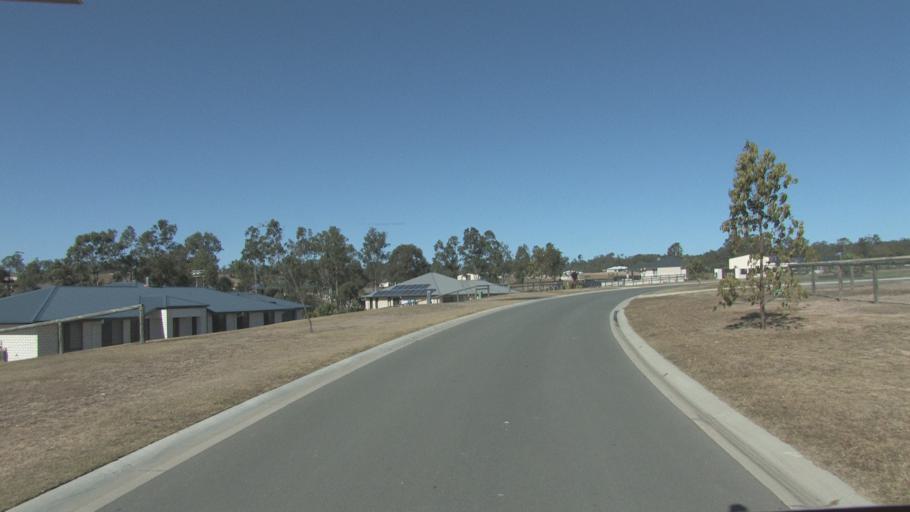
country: AU
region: Queensland
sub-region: Logan
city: Cedar Vale
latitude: -27.8700
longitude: 153.0456
